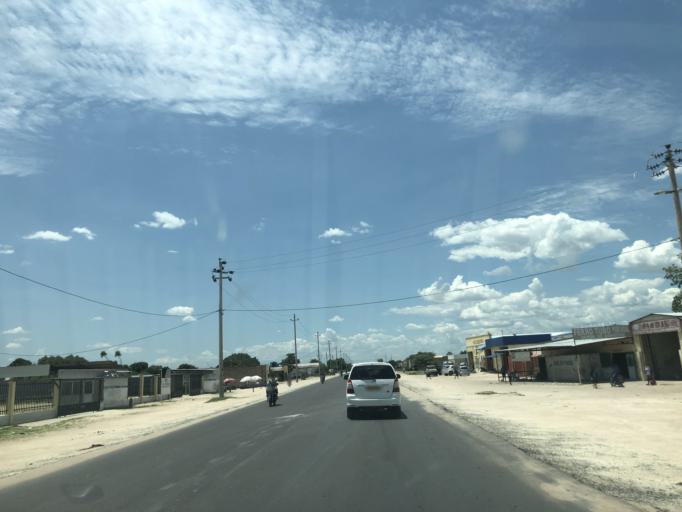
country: AO
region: Cunene
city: Ondjiva
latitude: -17.0529
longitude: 15.7426
